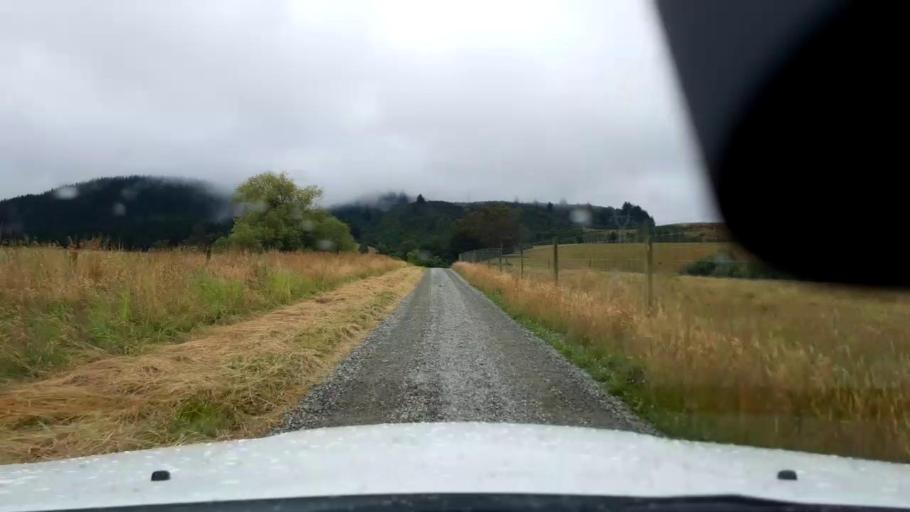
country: NZ
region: Canterbury
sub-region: Timaru District
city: Pleasant Point
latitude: -44.0761
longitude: 171.1437
